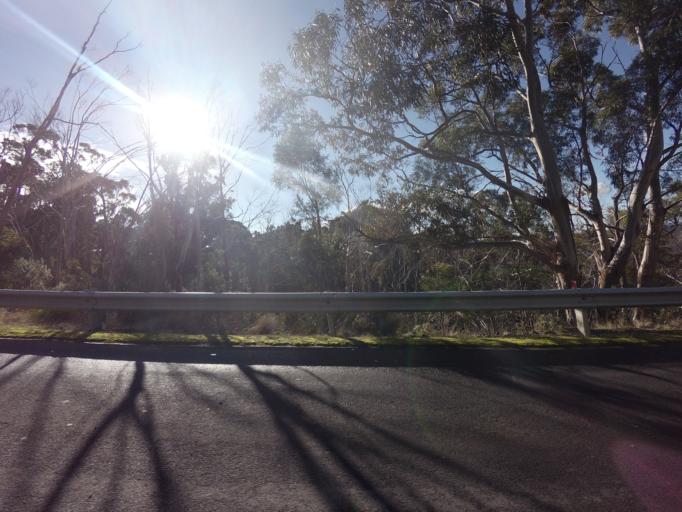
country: AU
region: Tasmania
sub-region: Glenorchy
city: Berriedale
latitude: -42.8225
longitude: 147.2048
